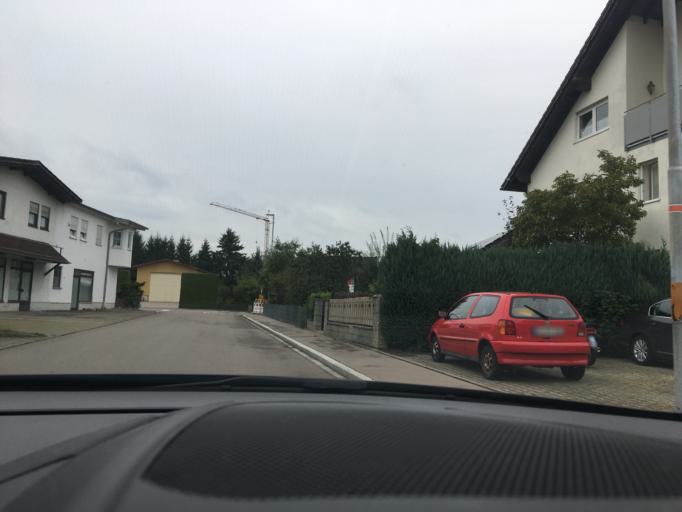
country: DE
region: Baden-Wuerttemberg
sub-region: Tuebingen Region
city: Kirchdorf
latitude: 48.0808
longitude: 10.1246
